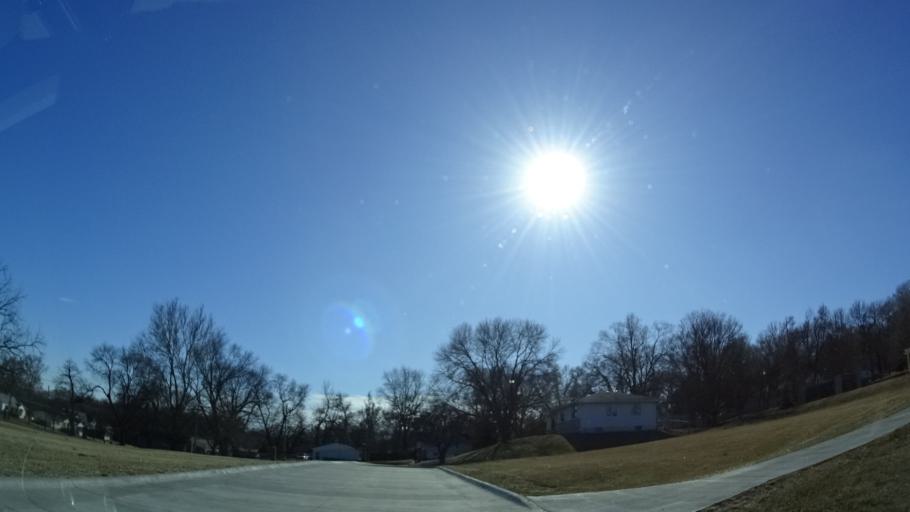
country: US
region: Nebraska
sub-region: Sarpy County
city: Bellevue
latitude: 41.1490
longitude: -95.8917
